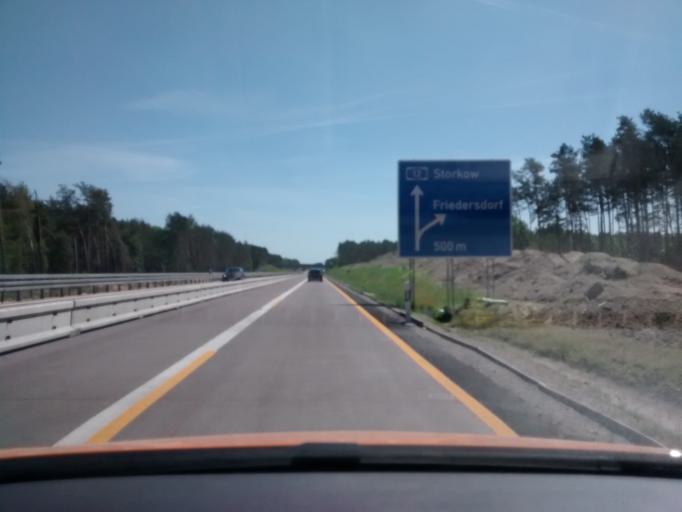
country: DE
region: Brandenburg
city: Erkner
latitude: 52.3215
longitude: 13.7711
